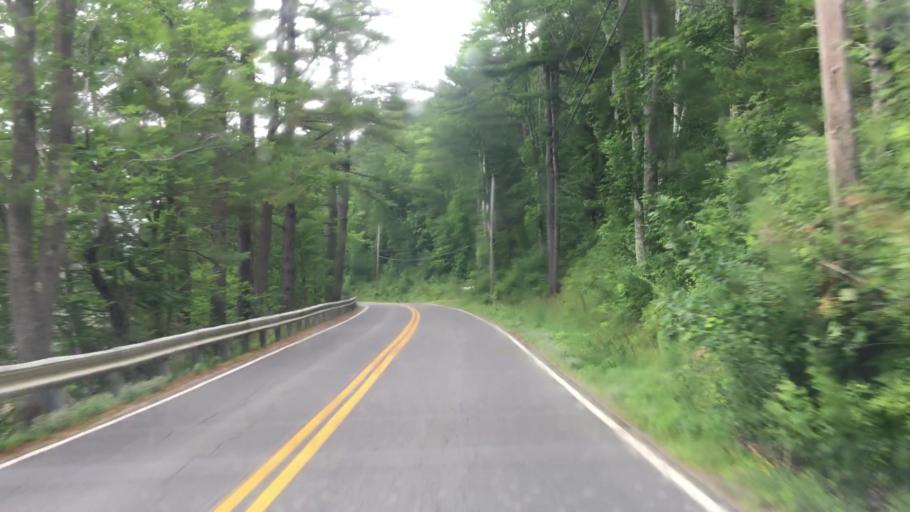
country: US
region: Maine
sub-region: Lincoln County
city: Wiscasset
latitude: 43.9914
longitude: -69.6488
